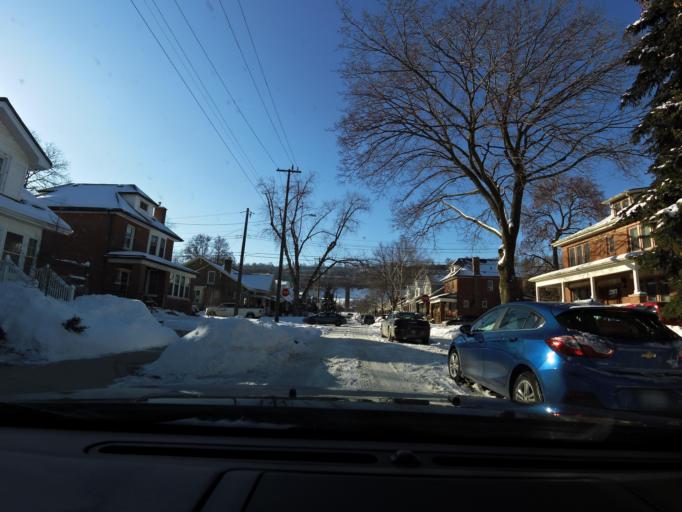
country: CA
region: Ontario
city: Hamilton
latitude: 43.2381
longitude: -79.8250
